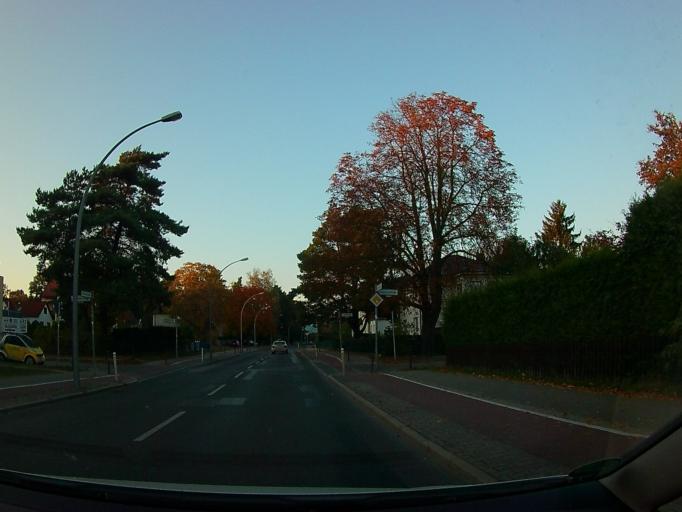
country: DE
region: Berlin
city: Bohnsdorf
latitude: 52.4026
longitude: 13.5737
